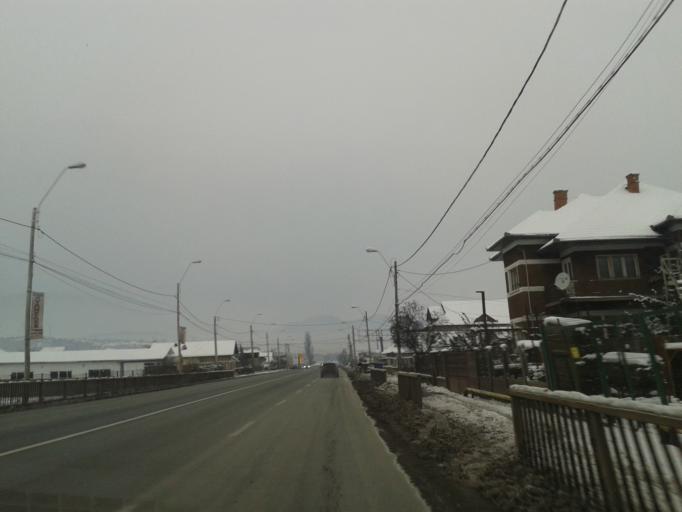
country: RO
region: Hunedoara
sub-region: Municipiul Deva
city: Cristur
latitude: 45.8568
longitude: 22.9498
